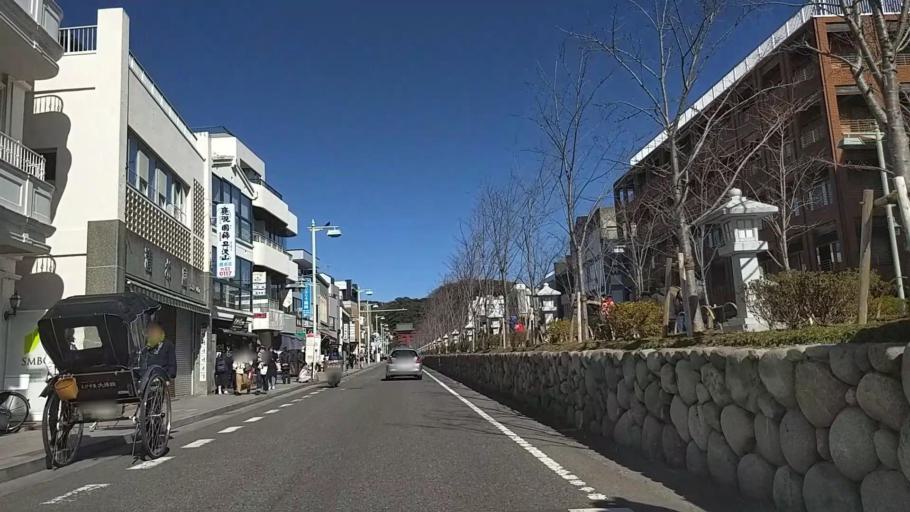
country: JP
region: Kanagawa
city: Kamakura
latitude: 35.3218
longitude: 139.5537
